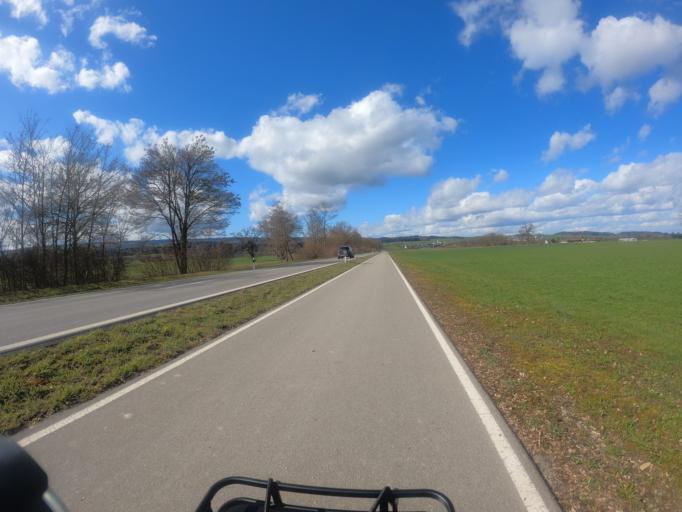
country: CH
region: Zurich
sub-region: Bezirk Affoltern
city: Ottenbach
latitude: 47.2796
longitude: 8.3888
